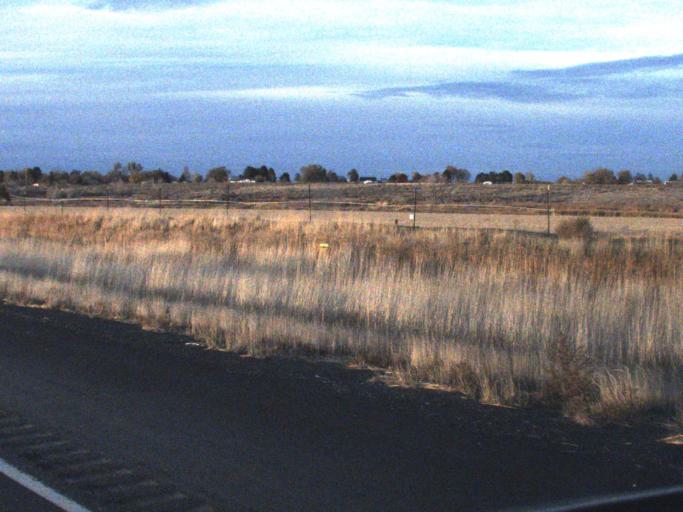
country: US
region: Washington
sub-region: Walla Walla County
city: Burbank
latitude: 46.2002
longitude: -118.9998
